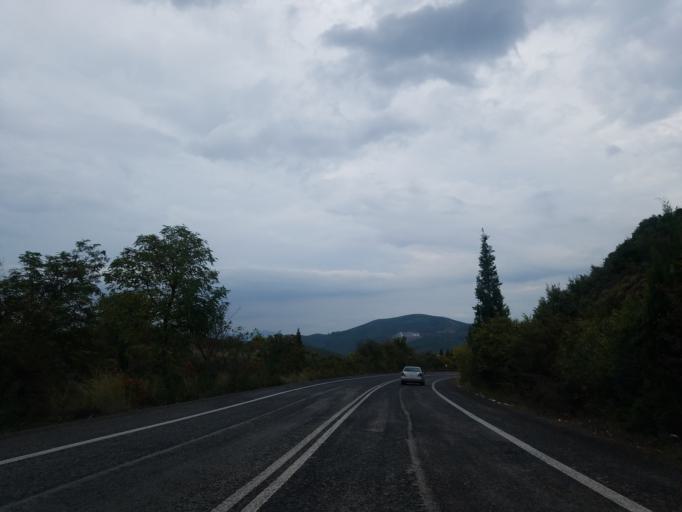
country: GR
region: Central Greece
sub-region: Nomos Voiotias
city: Stirion
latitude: 38.4495
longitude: 22.7846
